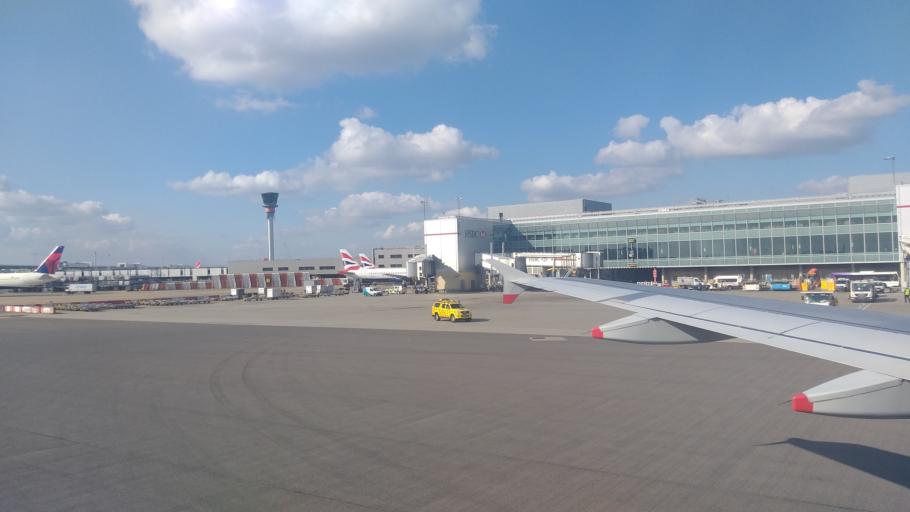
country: GB
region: England
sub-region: Greater London
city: West Drayton
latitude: 51.4674
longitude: -0.4575
